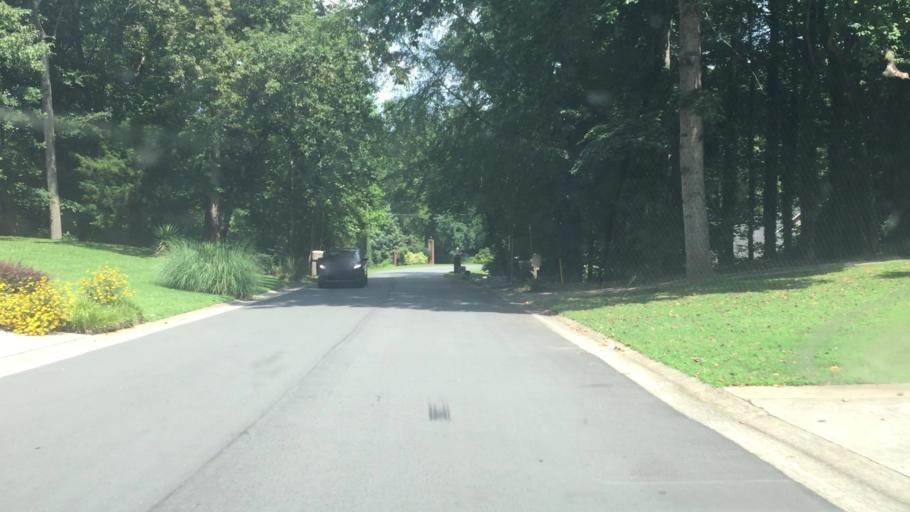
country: US
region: North Carolina
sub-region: Iredell County
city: Mooresville
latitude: 35.5528
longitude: -80.7992
